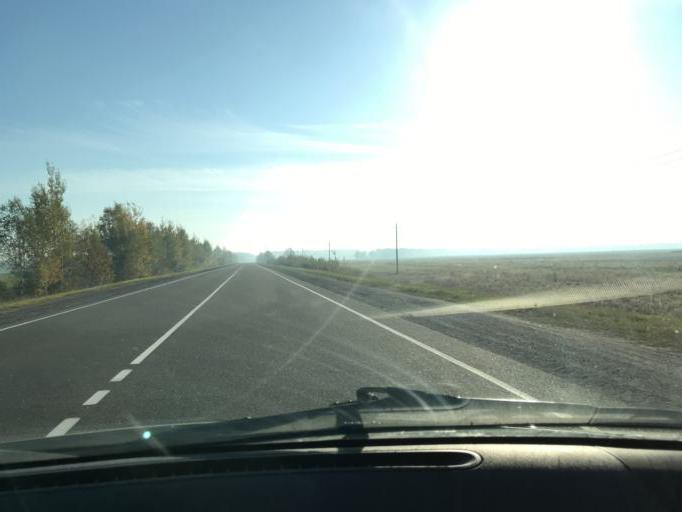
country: BY
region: Brest
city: Horad Luninyets
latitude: 52.3138
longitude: 26.6514
